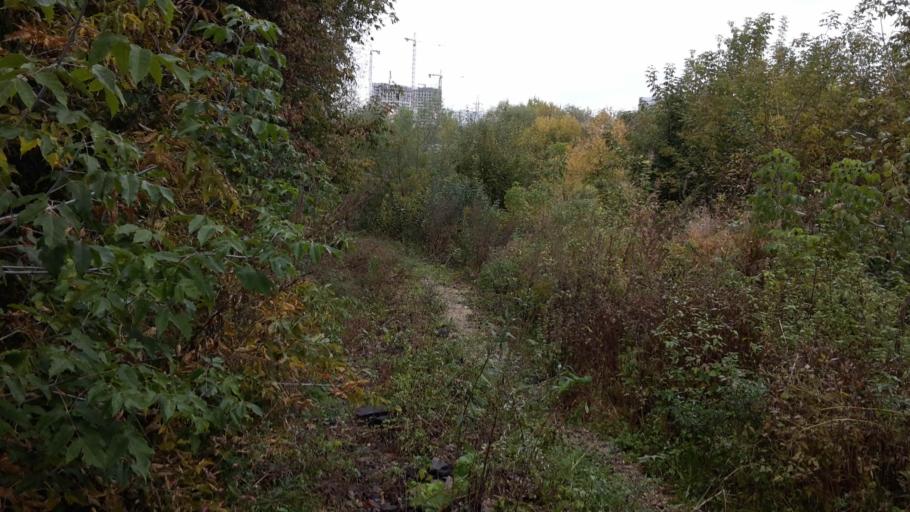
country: RU
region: Moskovskaya
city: Kur'yanovo
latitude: 55.6390
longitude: 37.7030
